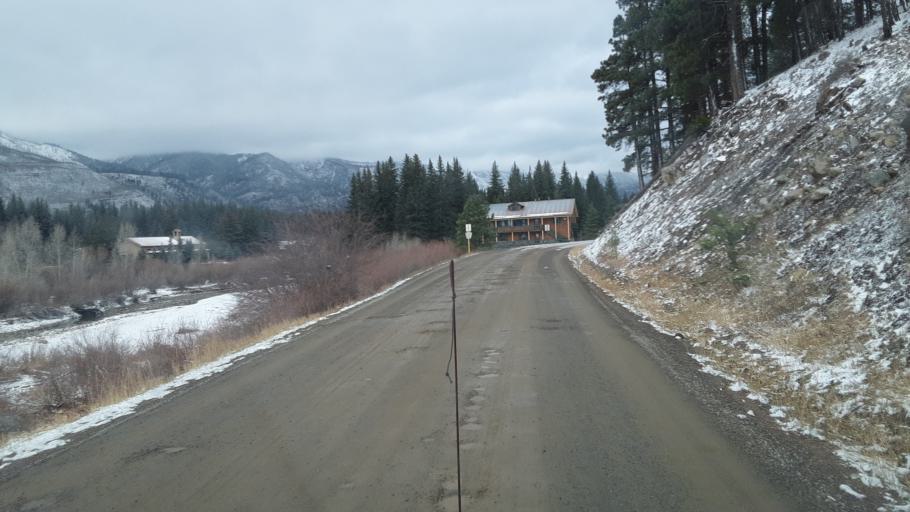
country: US
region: Colorado
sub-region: La Plata County
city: Bayfield
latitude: 37.4339
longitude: -107.5430
